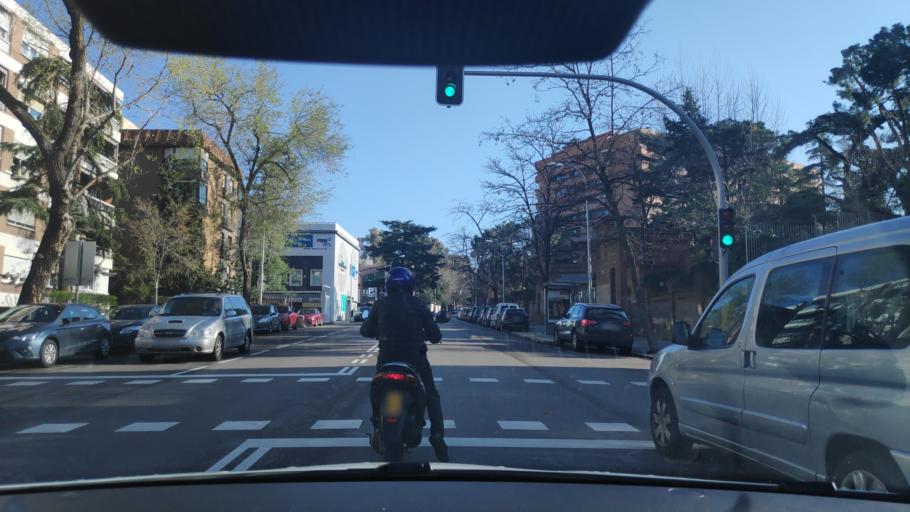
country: ES
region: Madrid
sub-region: Provincia de Madrid
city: Chamartin
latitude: 40.4532
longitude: -3.6847
